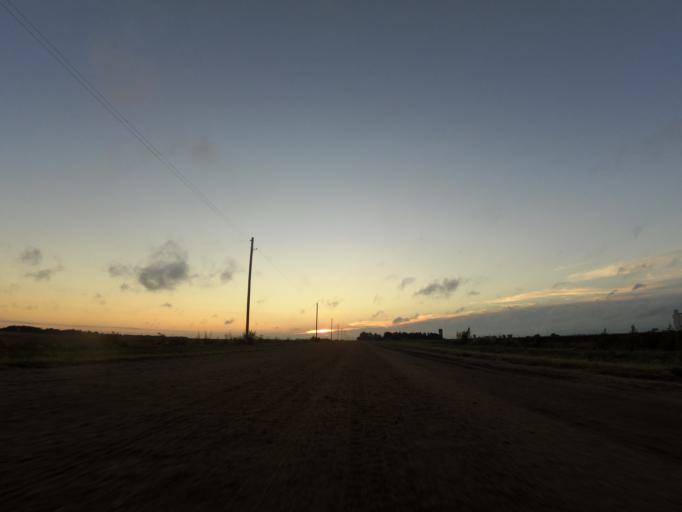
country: US
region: Kansas
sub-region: Reno County
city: South Hutchinson
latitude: 38.0135
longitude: -98.0230
